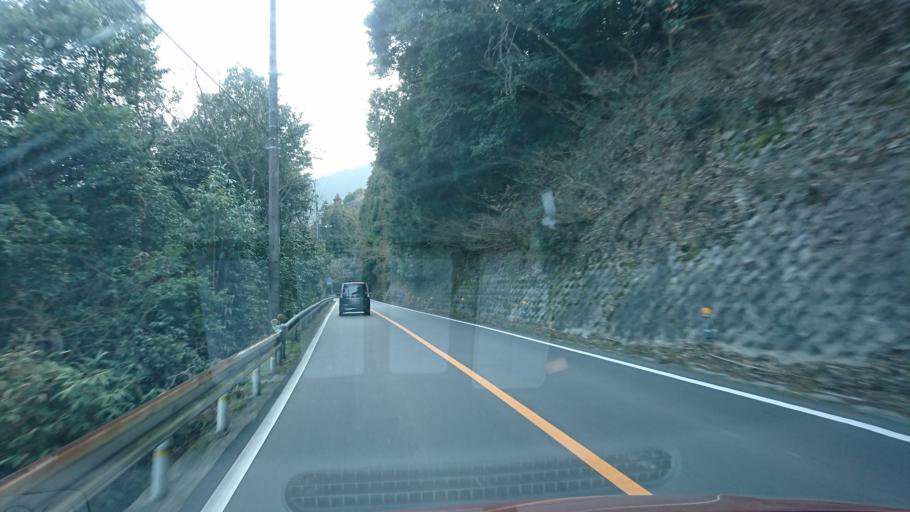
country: JP
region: Ehime
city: Hojo
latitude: 33.9733
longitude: 132.9026
